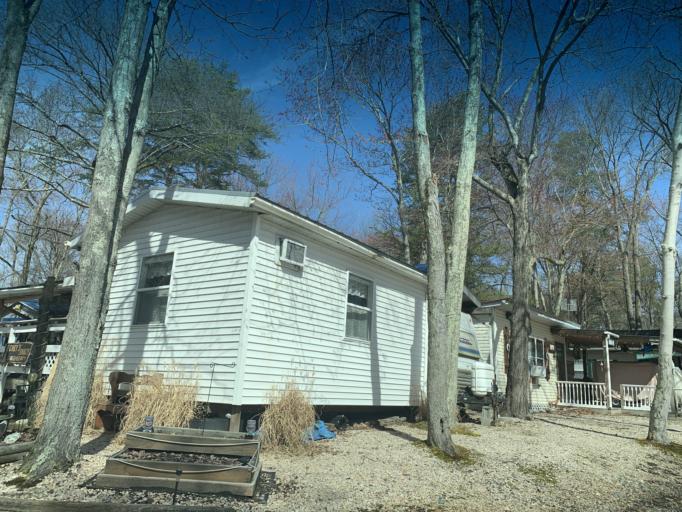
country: US
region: Maryland
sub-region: Cecil County
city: Charlestown
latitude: 39.5519
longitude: -76.0093
